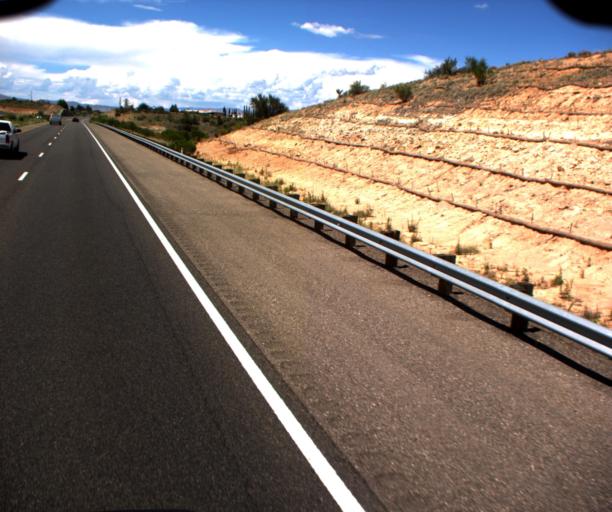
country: US
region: Arizona
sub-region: Yavapai County
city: Verde Village
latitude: 34.6844
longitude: -111.9770
